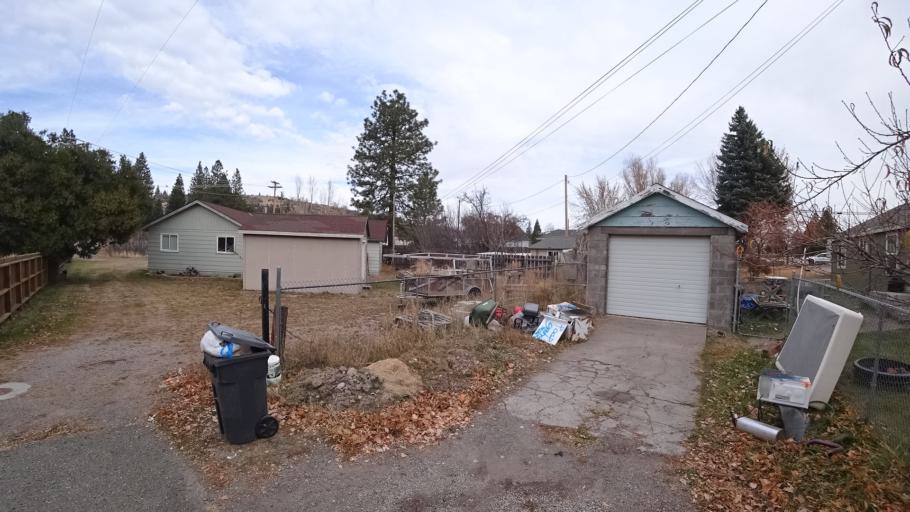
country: US
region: California
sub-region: Siskiyou County
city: Weed
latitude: 41.4291
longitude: -122.3886
